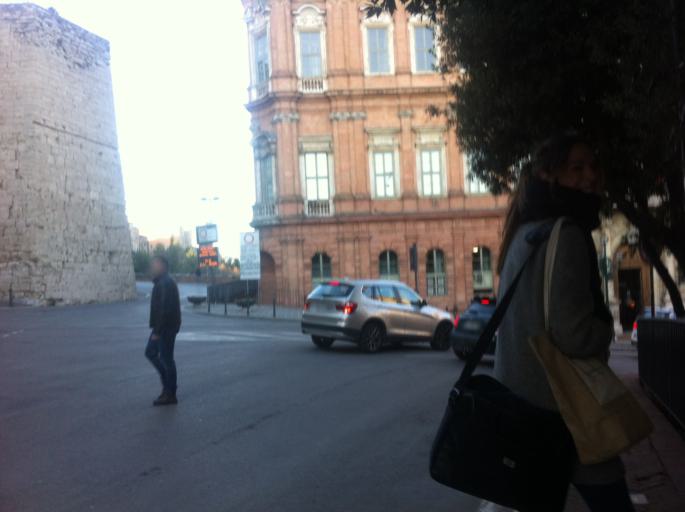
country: IT
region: Umbria
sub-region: Provincia di Perugia
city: Perugia
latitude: 43.1140
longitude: 12.3919
